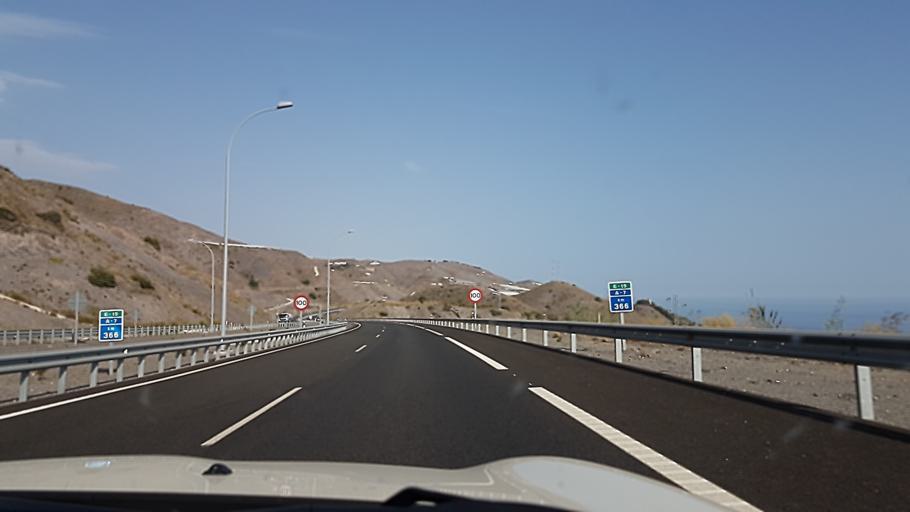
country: ES
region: Andalusia
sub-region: Provincia de Granada
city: Sorvilan
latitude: 36.7570
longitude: -3.2463
